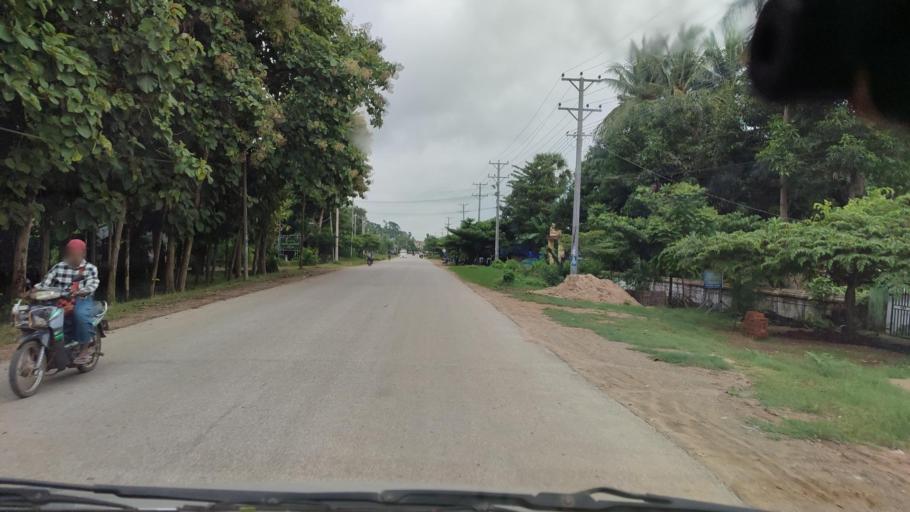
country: MM
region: Bago
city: Pyay
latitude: 18.8524
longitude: 95.3918
